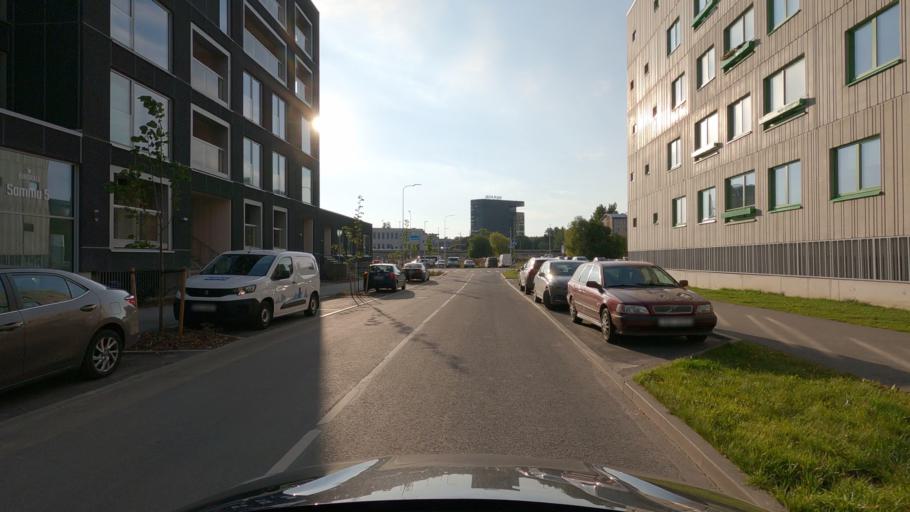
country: EE
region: Harju
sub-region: Tallinna linn
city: Tallinn
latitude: 59.4060
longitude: 24.7252
